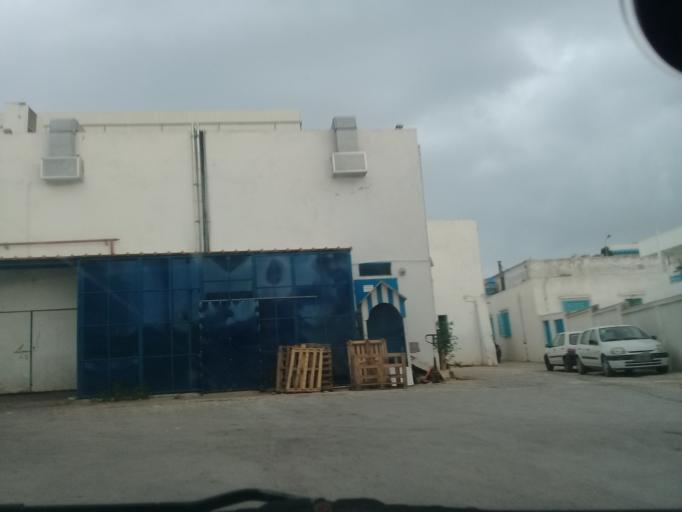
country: TN
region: Tunis
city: Sidi Bou Said
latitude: 36.8699
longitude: 10.3427
